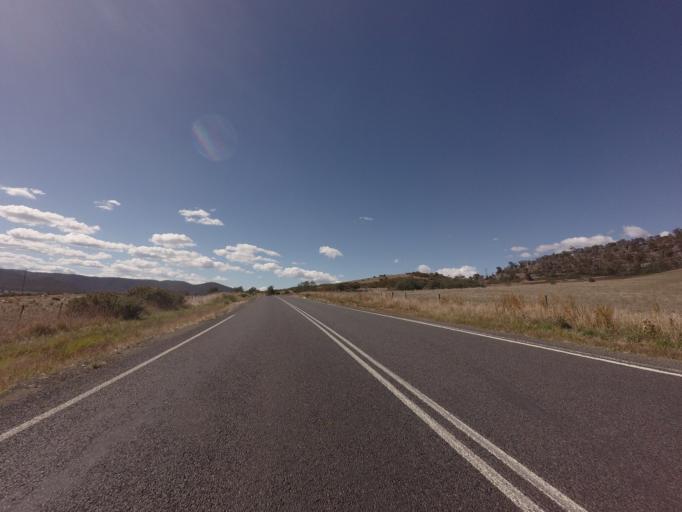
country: AU
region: Tasmania
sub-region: Break O'Day
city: St Helens
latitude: -41.6982
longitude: 147.8611
